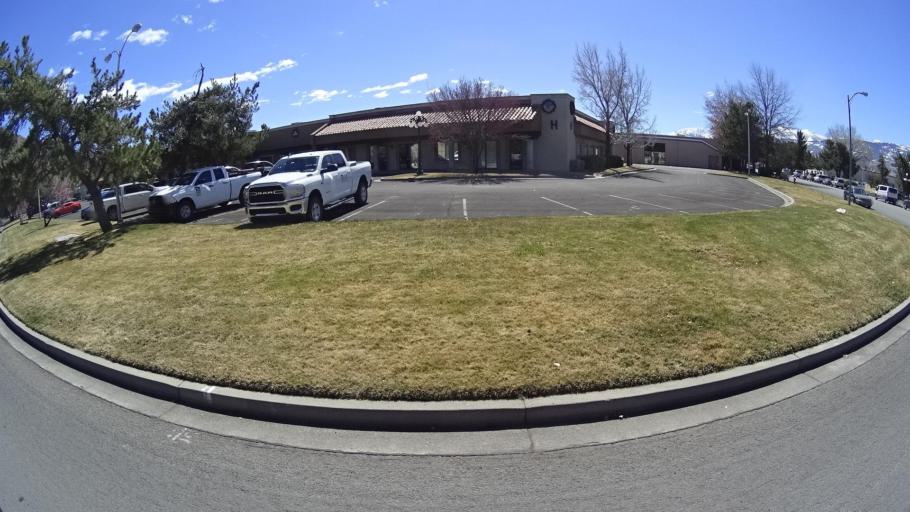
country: US
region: Nevada
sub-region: Washoe County
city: Sparks
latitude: 39.4749
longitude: -119.7674
